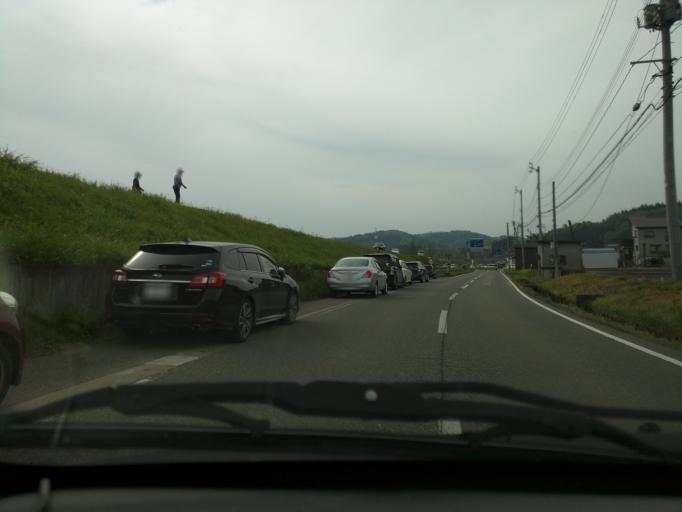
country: JP
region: Niigata
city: Ojiya
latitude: 37.2526
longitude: 138.9225
